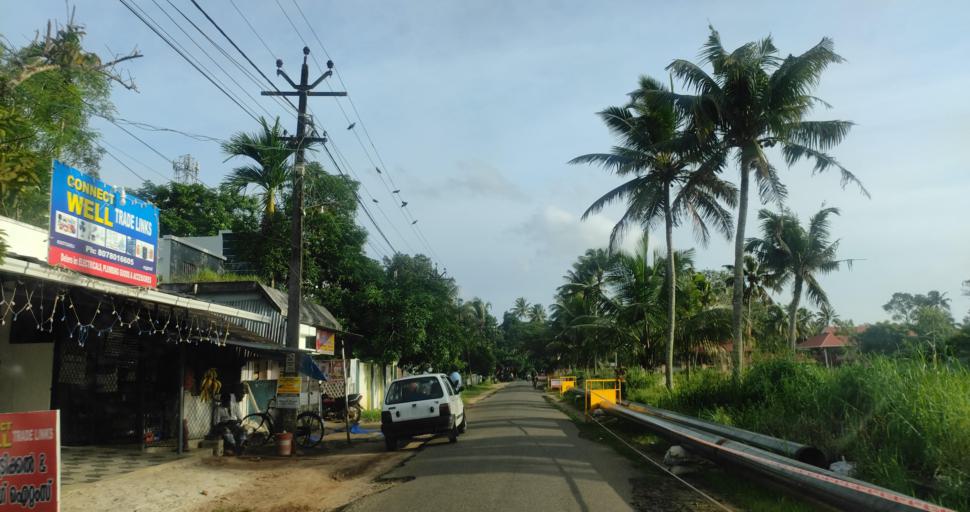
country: IN
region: Kerala
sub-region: Alappuzha
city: Shertallai
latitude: 9.6361
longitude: 76.3434
